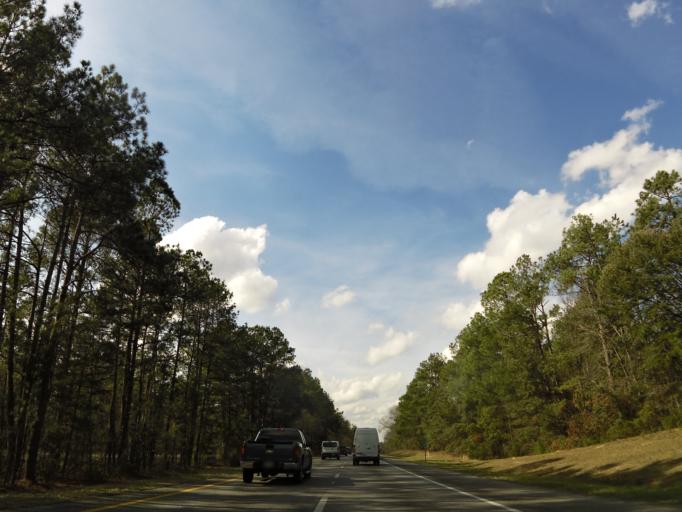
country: US
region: South Carolina
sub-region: Dorchester County
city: Ridgeville
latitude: 33.1535
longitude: -80.3438
